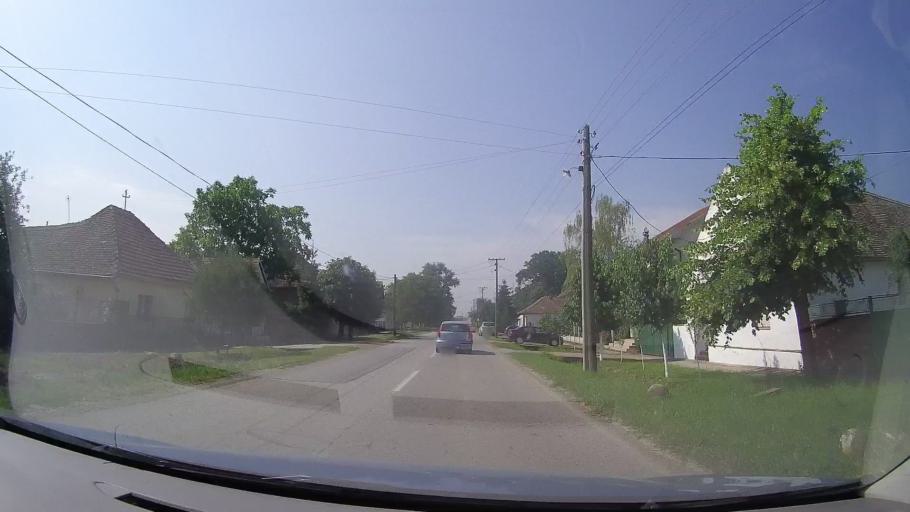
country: RS
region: Autonomna Pokrajina Vojvodina
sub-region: Srednjebanatski Okrug
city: Secanj
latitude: 45.3626
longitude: 20.7717
